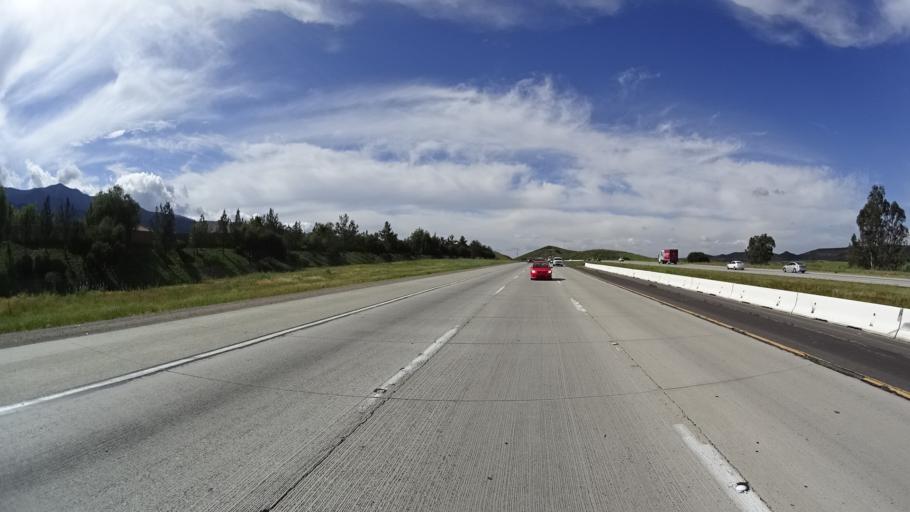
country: US
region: California
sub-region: Riverside County
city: El Cerrito
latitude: 33.7642
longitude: -117.4757
